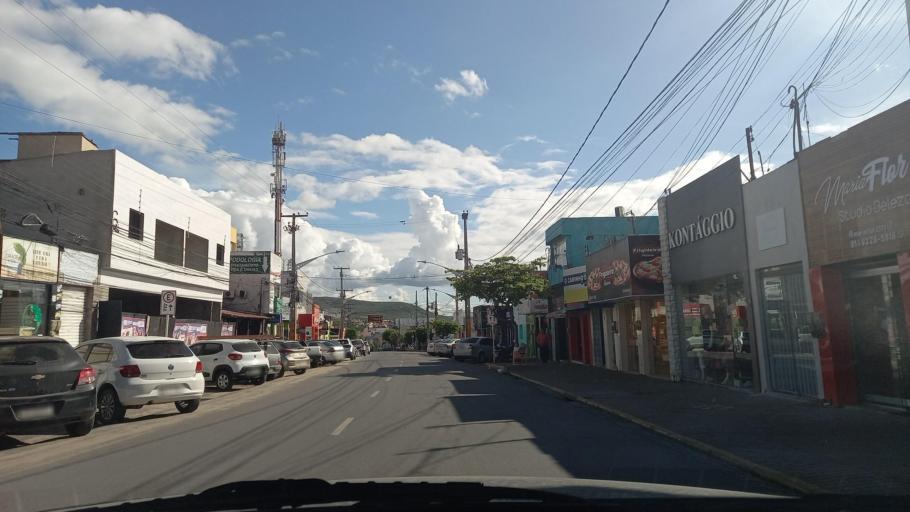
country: BR
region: Pernambuco
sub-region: Gravata
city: Gravata
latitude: -8.1997
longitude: -35.5638
